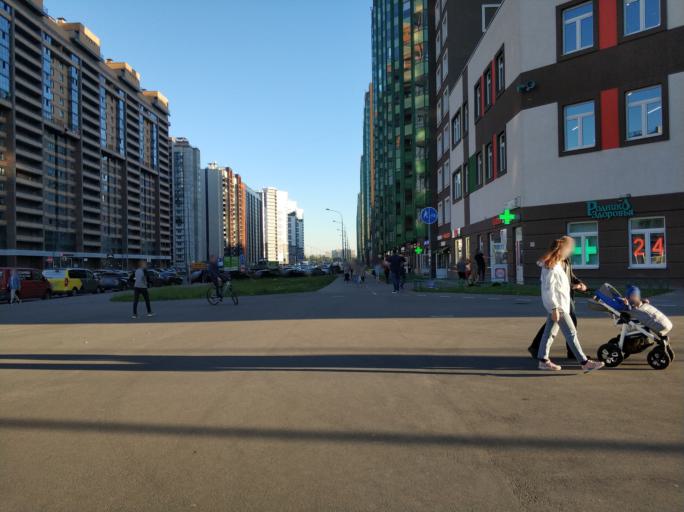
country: RU
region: Leningrad
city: Murino
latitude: 60.0577
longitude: 30.4286
